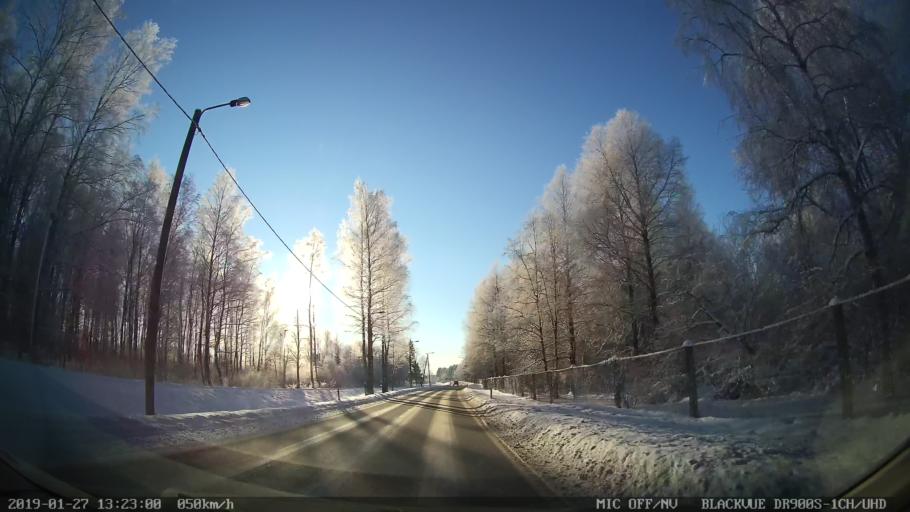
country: EE
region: Harju
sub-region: Tallinna linn
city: Tallinn
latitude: 59.4092
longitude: 24.7981
